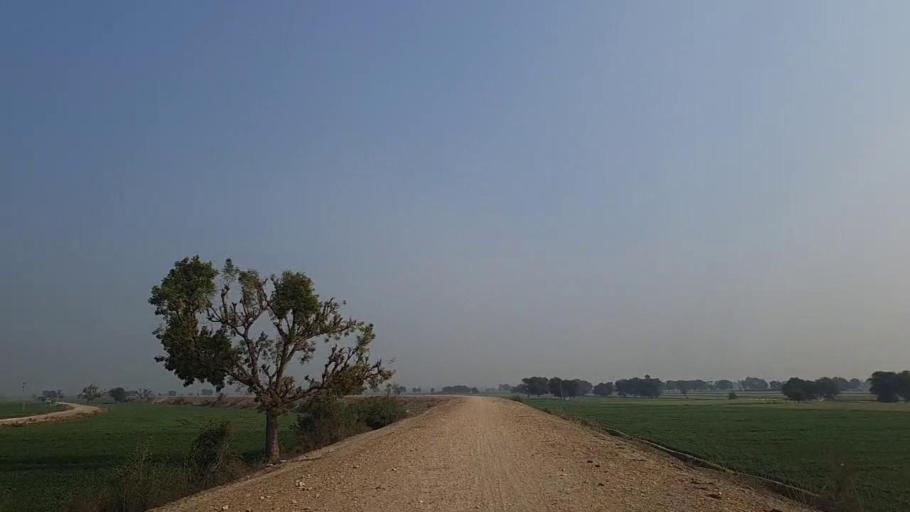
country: PK
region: Sindh
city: Sann
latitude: 26.0872
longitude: 68.1568
